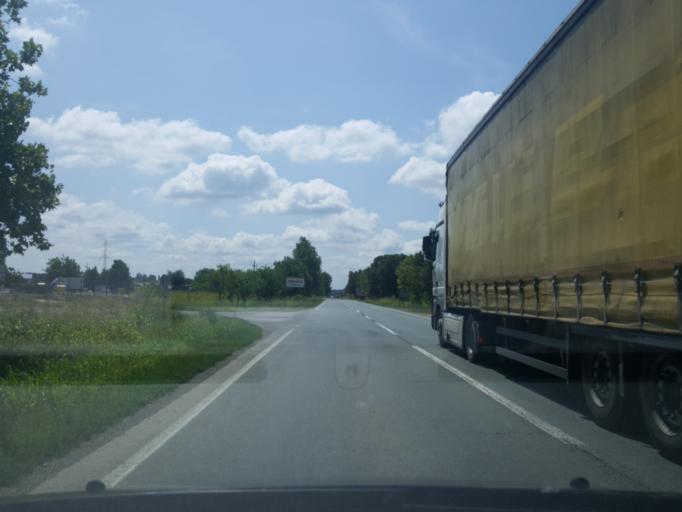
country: RS
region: Autonomna Pokrajina Vojvodina
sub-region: Sremski Okrug
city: Sremska Mitrovica
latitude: 44.9805
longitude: 19.6389
